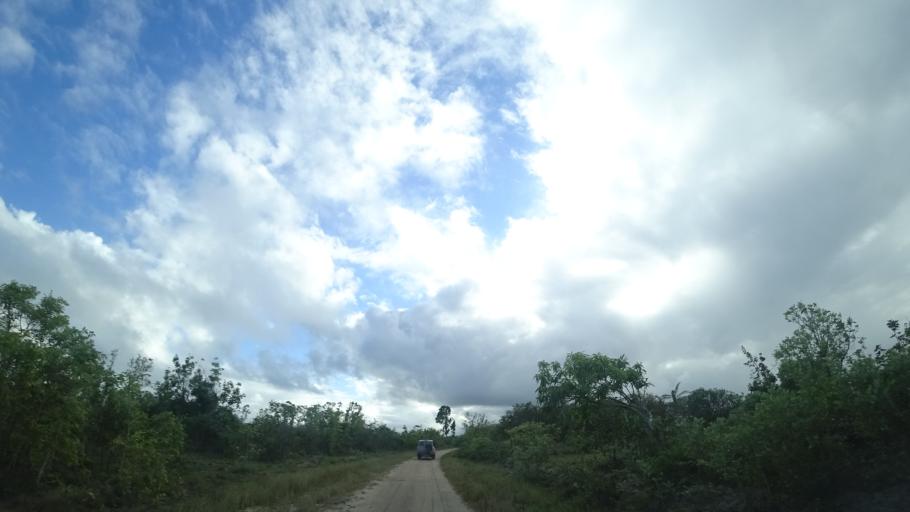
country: MZ
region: Sofala
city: Beira
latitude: -19.6666
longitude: 35.0583
